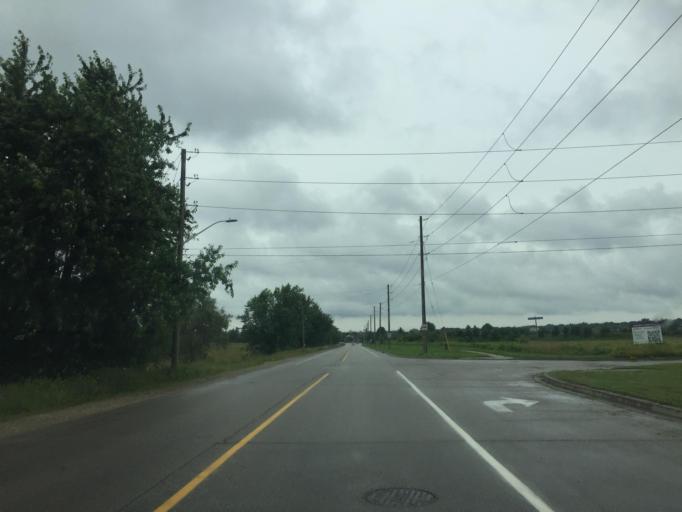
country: CA
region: Ontario
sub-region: Wellington County
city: Guelph
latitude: 43.4924
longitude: -80.2321
